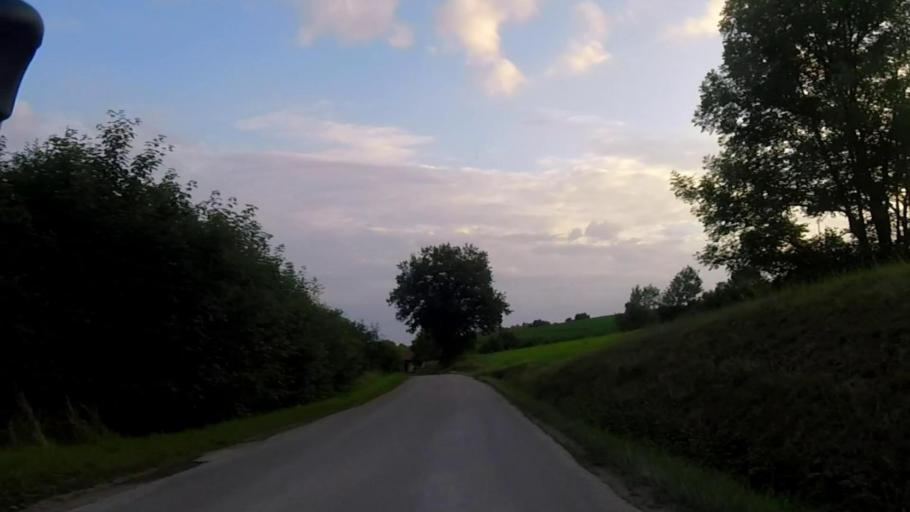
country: DE
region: Baden-Wuerttemberg
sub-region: Regierungsbezirk Stuttgart
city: Oberstenfeld
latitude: 49.0049
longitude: 9.3657
